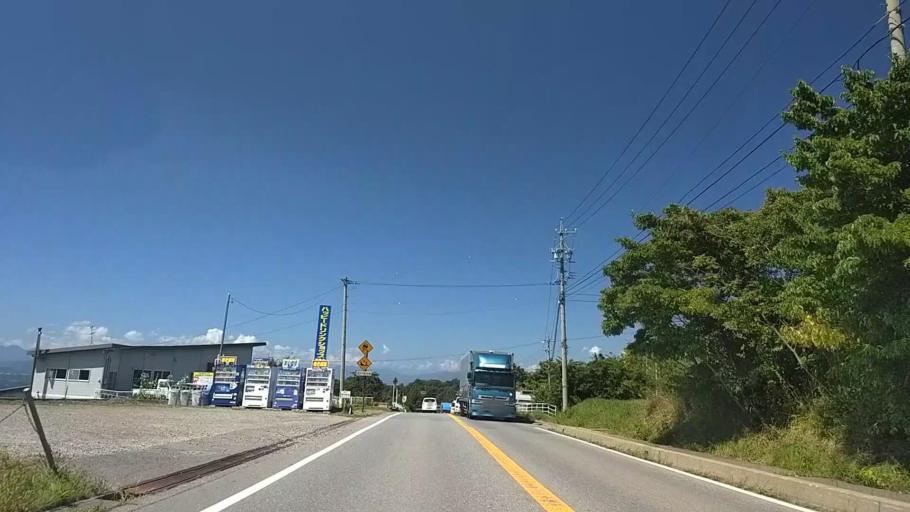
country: JP
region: Nagano
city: Komoro
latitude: 36.3506
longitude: 138.4180
